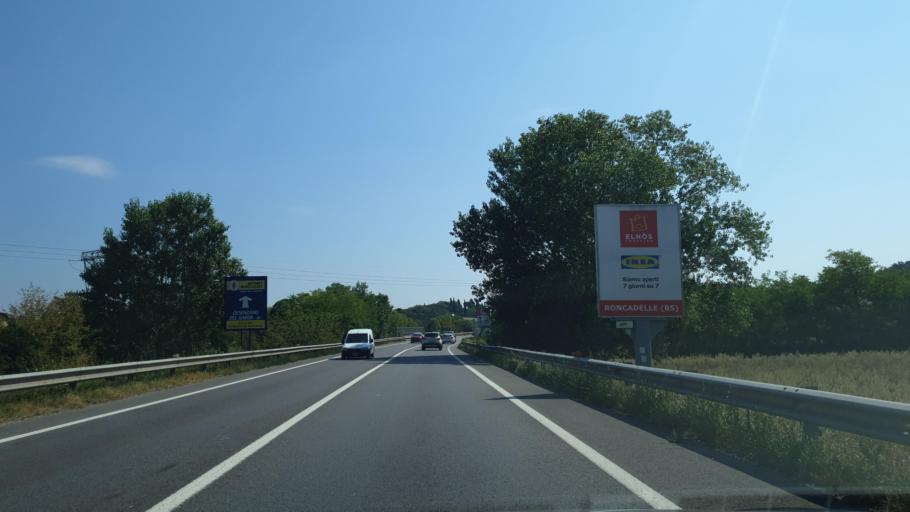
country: IT
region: Lombardy
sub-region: Provincia di Brescia
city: Lonato
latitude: 45.4669
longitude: 10.4995
